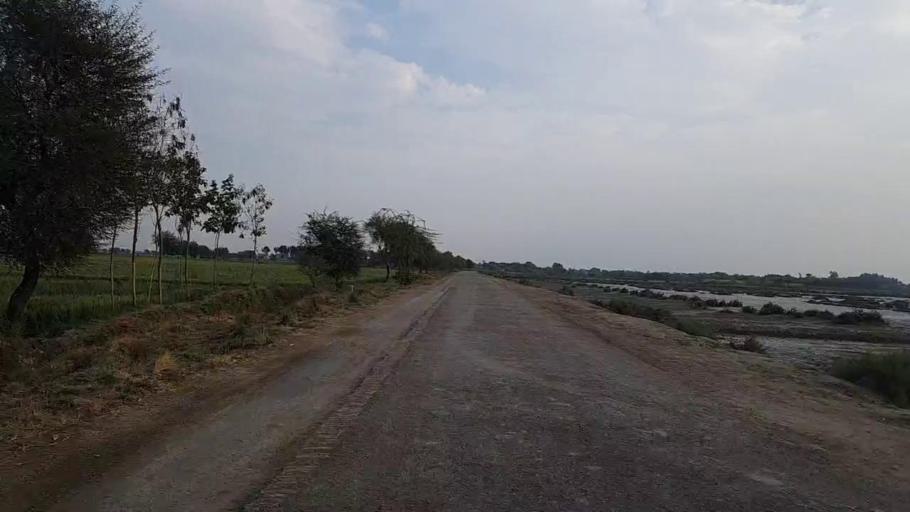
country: PK
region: Sindh
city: Pithoro
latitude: 25.4665
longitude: 69.2740
